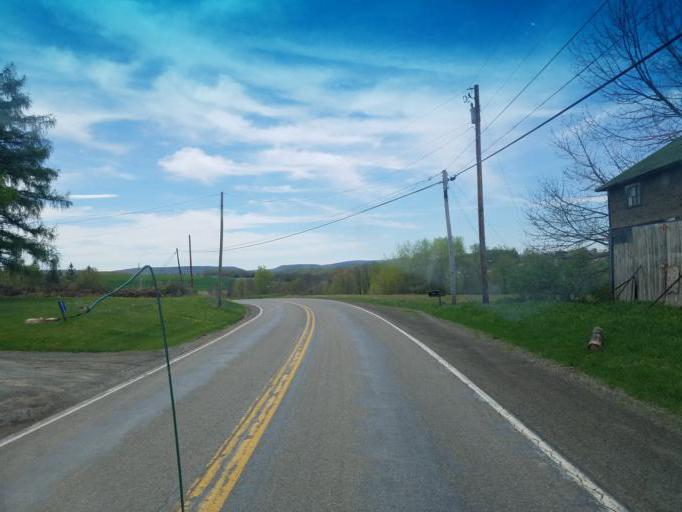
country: US
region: Pennsylvania
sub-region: Tioga County
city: Wellsboro
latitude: 41.7160
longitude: -77.3823
